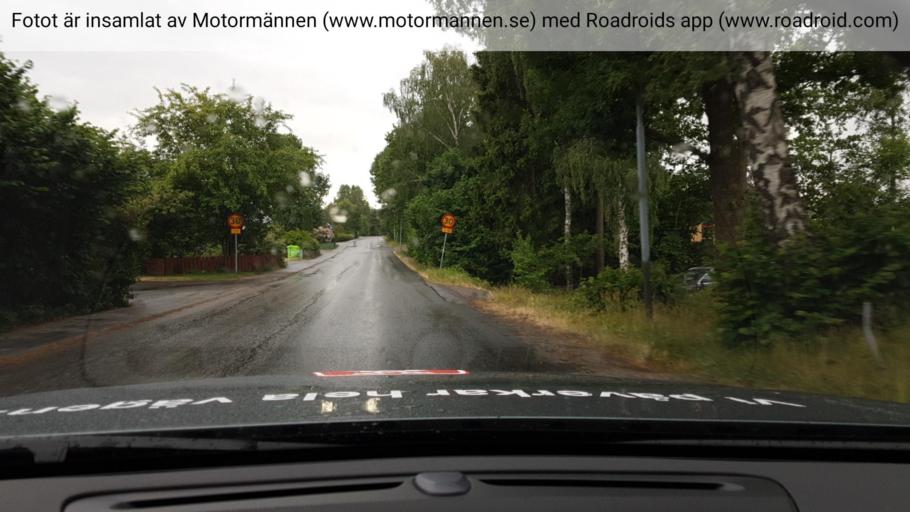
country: SE
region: Stockholm
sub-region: Vallentuna Kommun
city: Vallentuna
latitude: 59.5205
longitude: 18.0706
